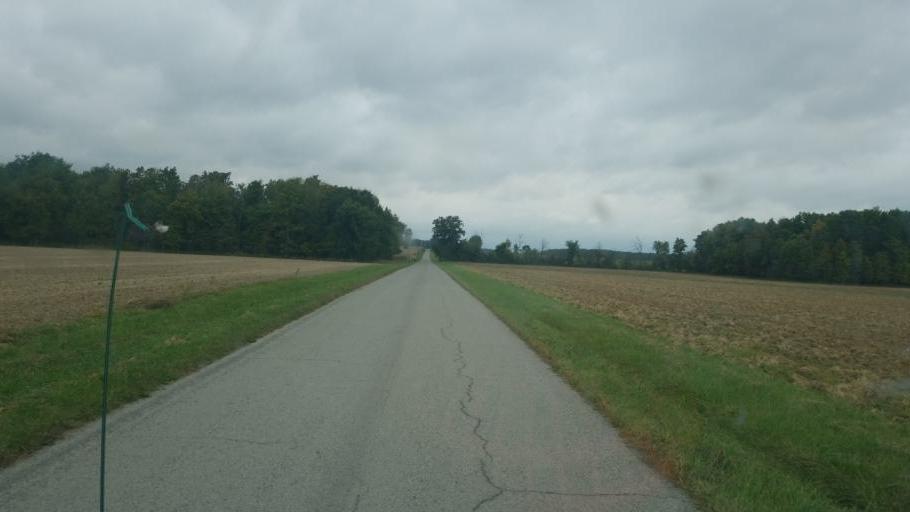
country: US
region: Ohio
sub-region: Seneca County
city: Fostoria
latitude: 41.0691
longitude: -83.4961
